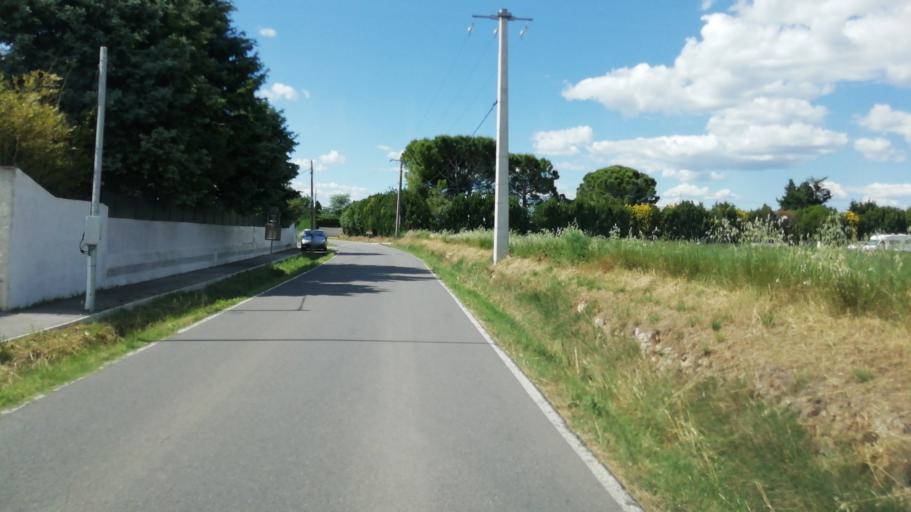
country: FR
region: Languedoc-Roussillon
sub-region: Departement de l'Herault
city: Saint-Just
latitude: 43.6618
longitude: 4.1109
